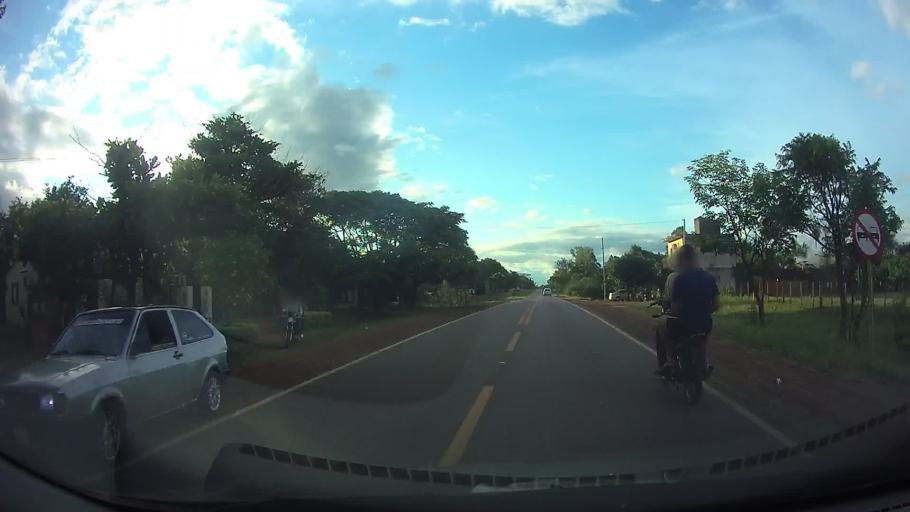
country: PY
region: Paraguari
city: Carapegua
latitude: -25.7973
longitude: -57.1981
